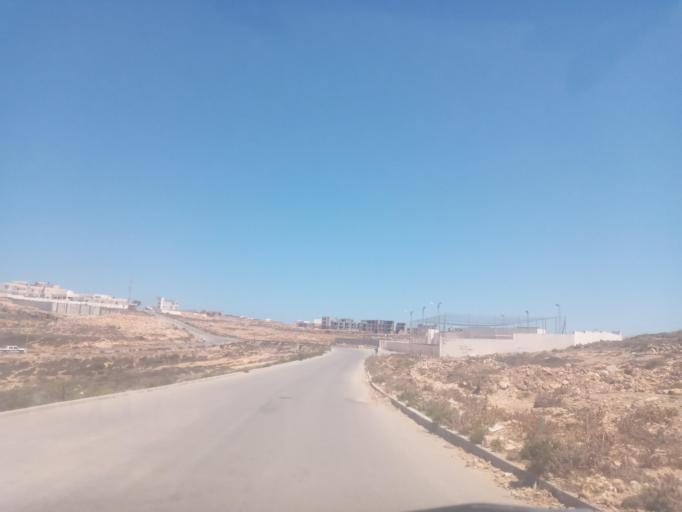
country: TN
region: Nabul
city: El Haouaria
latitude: 37.0558
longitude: 10.9947
